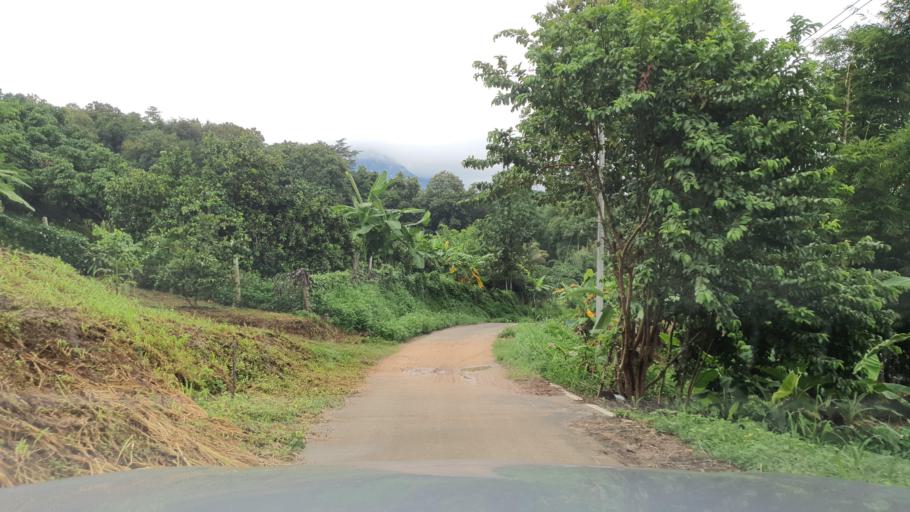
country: TH
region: Chiang Mai
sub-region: Amphoe Chiang Dao
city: Chiang Dao
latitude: 19.3335
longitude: 98.9281
